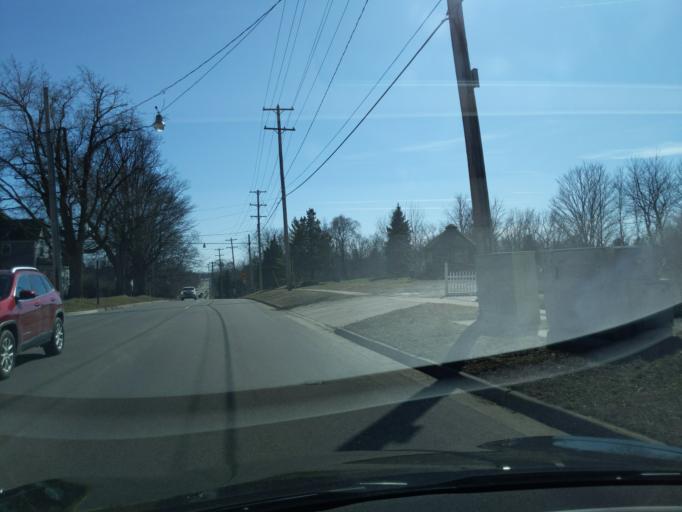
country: US
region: Michigan
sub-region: Ingham County
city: Mason
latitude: 42.5764
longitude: -84.4432
